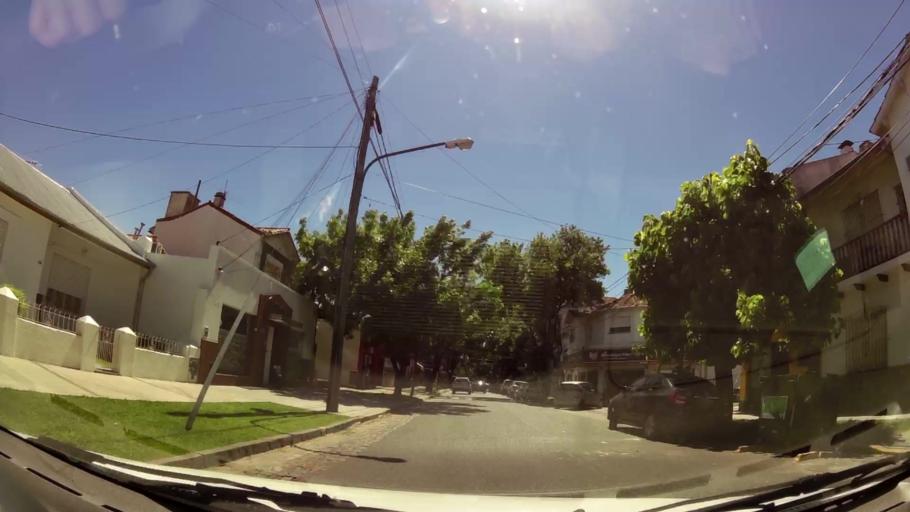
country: AR
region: Buenos Aires
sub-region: Partido de Vicente Lopez
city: Olivos
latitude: -34.5187
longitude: -58.5011
